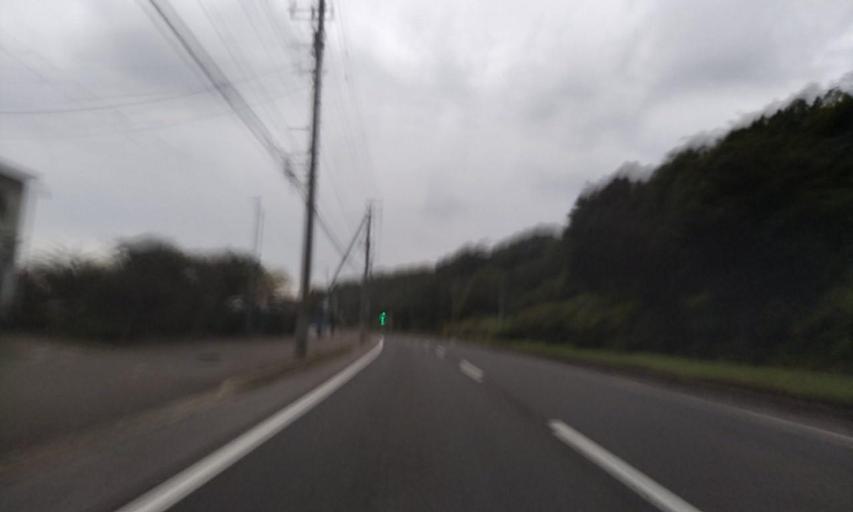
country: JP
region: Hokkaido
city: Abashiri
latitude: 43.9850
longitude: 144.2957
